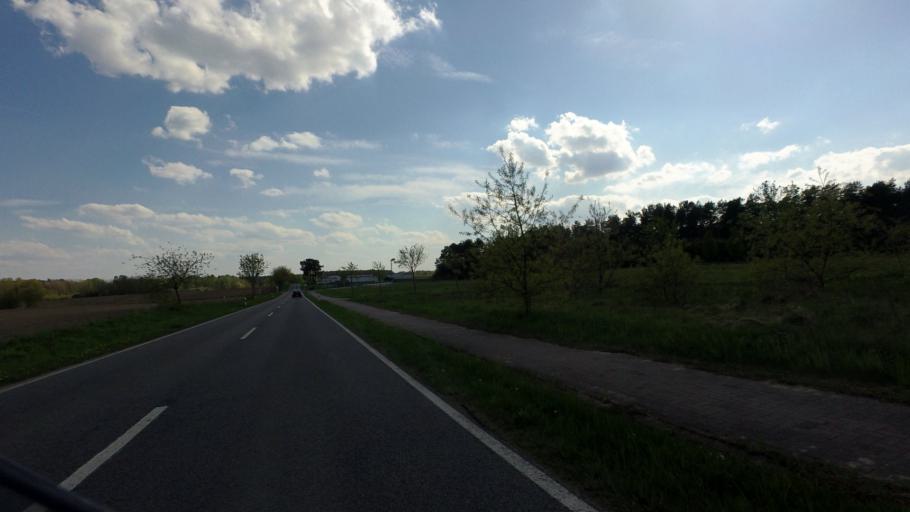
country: DE
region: Brandenburg
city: Templin
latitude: 53.1064
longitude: 13.5009
